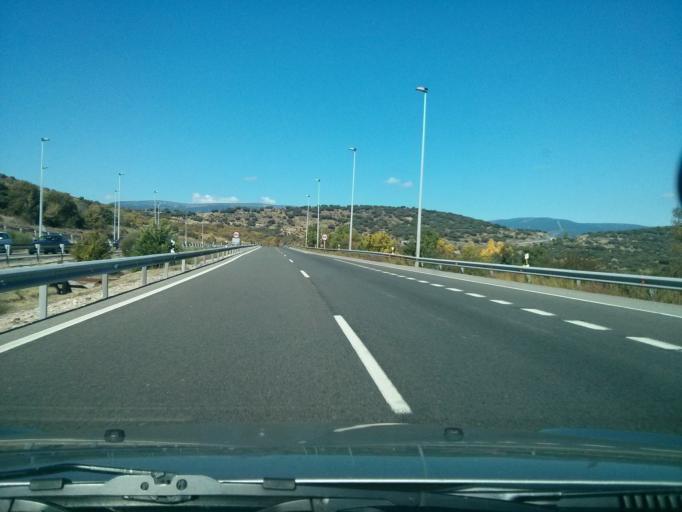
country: ES
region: Madrid
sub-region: Provincia de Madrid
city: Buitrago del Lozoya
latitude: 40.9430
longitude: -3.6328
